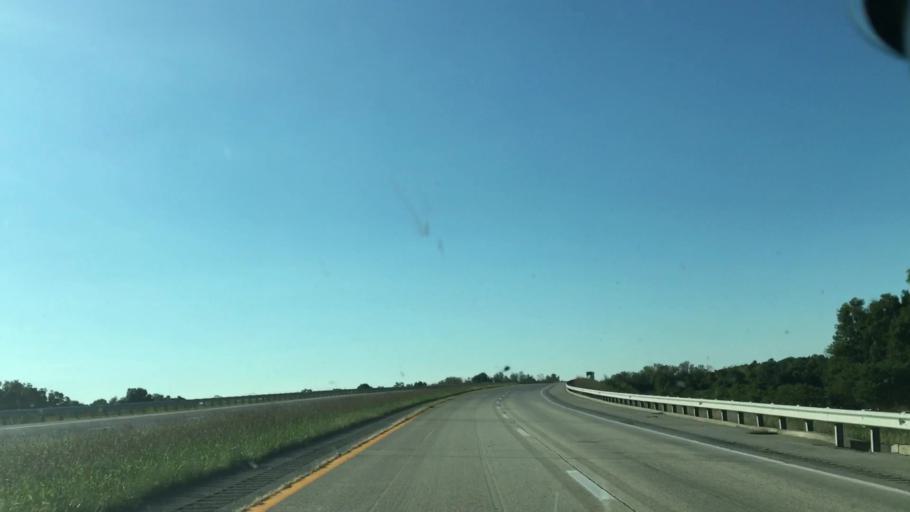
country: US
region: Kentucky
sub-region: Daviess County
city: Owensboro
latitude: 37.7533
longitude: -87.2931
